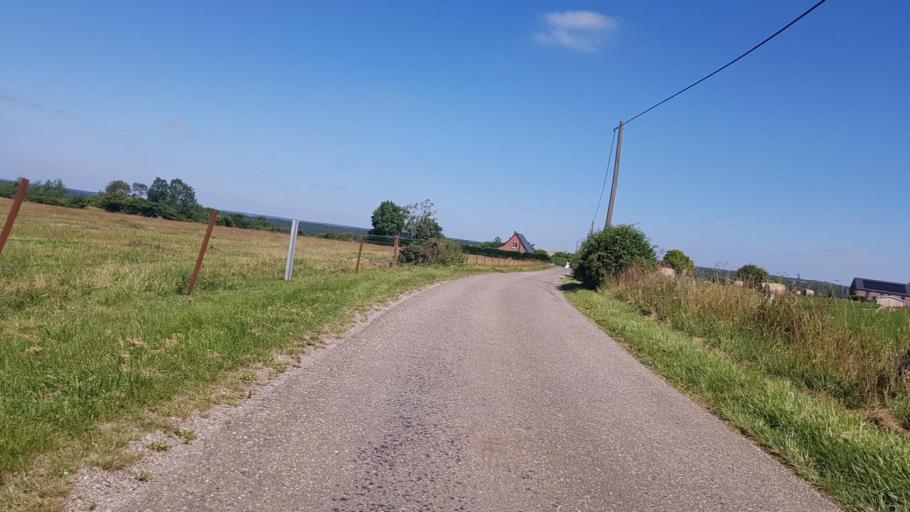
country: BE
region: Wallonia
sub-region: Province du Hainaut
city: Chimay
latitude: 50.0634
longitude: 4.2408
